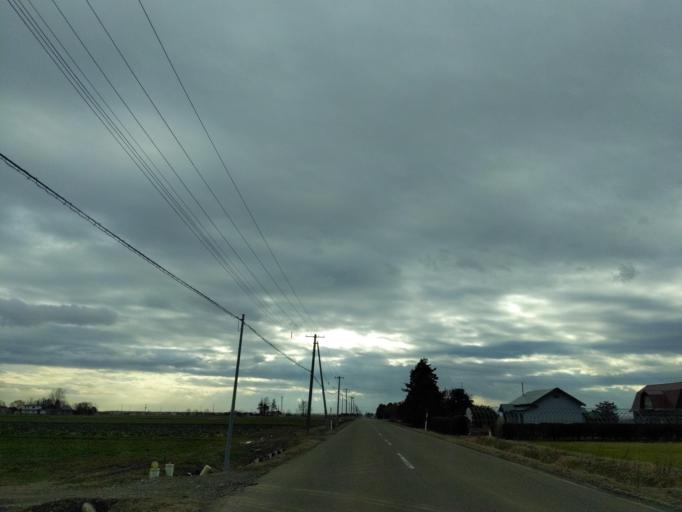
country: JP
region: Hokkaido
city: Kitahiroshima
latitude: 43.0391
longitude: 141.6893
